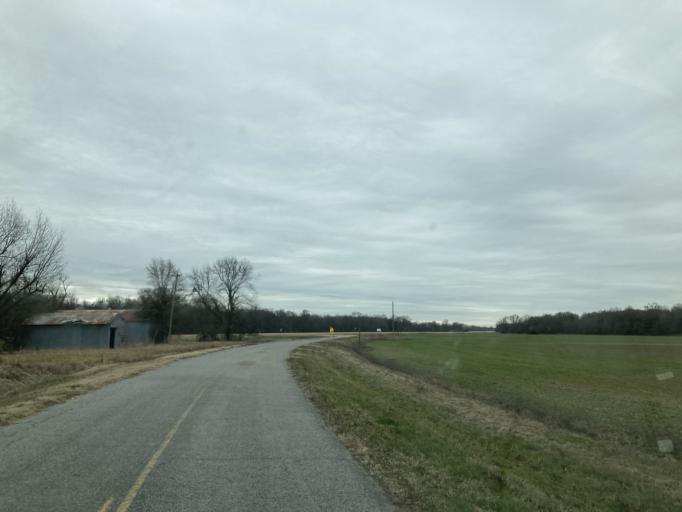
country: US
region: Mississippi
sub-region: Yazoo County
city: Yazoo City
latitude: 33.0115
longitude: -90.4710
